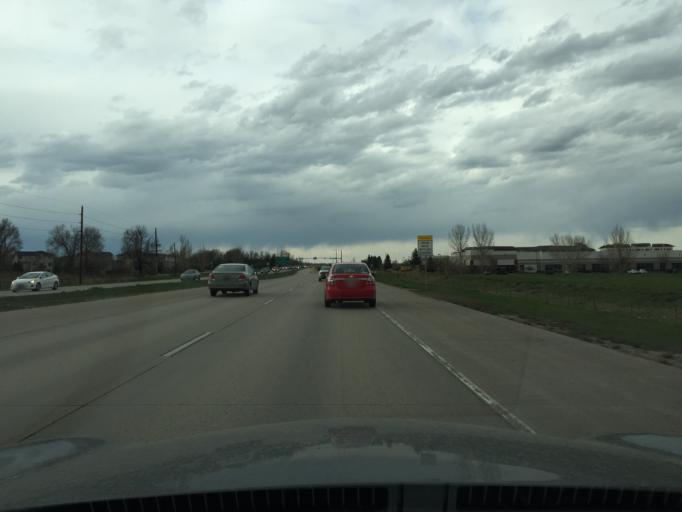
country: US
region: Colorado
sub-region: Boulder County
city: Lafayette
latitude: 39.9637
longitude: -105.0901
